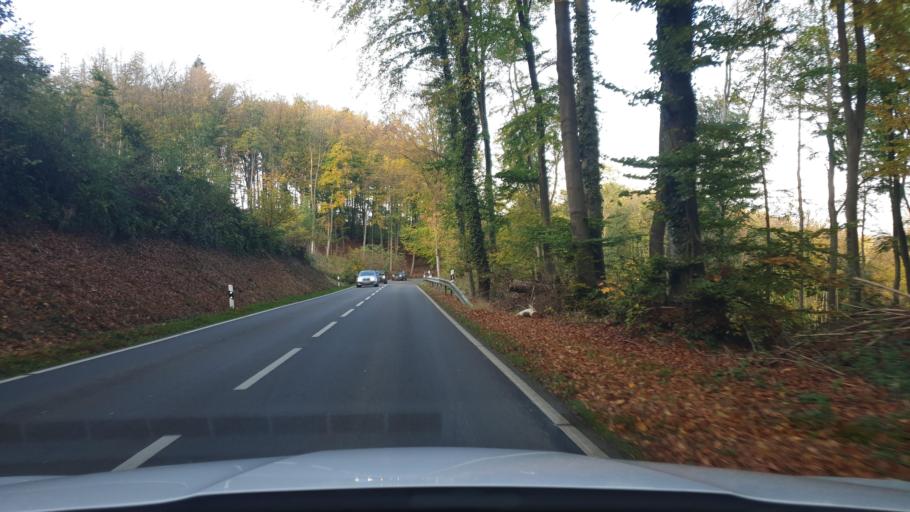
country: DE
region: North Rhine-Westphalia
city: Bad Oeynhausen
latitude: 52.2617
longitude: 8.8051
